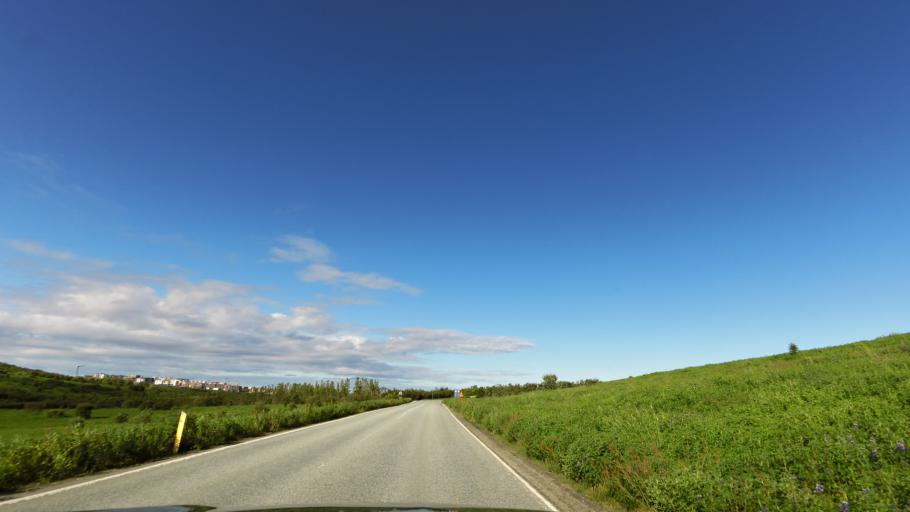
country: IS
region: Capital Region
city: Gardabaer
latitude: 64.0819
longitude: -21.8764
